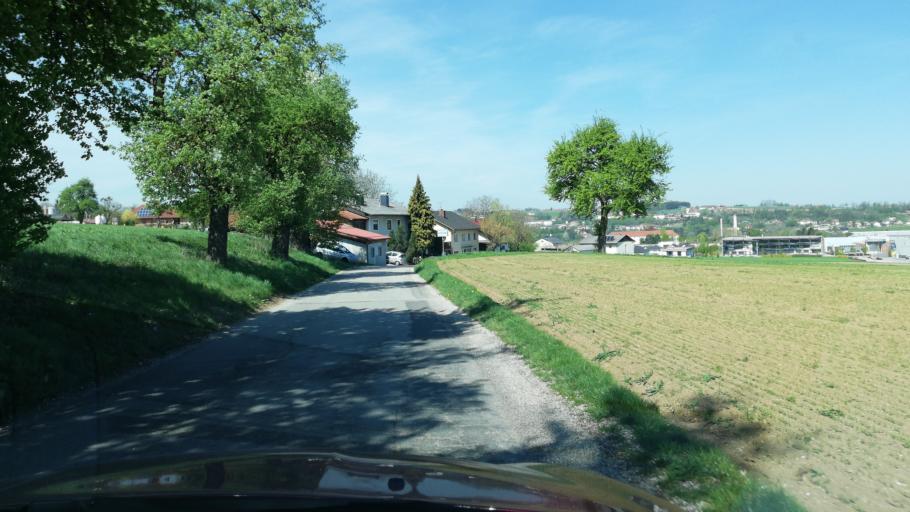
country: AT
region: Upper Austria
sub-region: Politischer Bezirk Kirchdorf an der Krems
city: Kremsmunster
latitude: 48.0487
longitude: 14.1547
